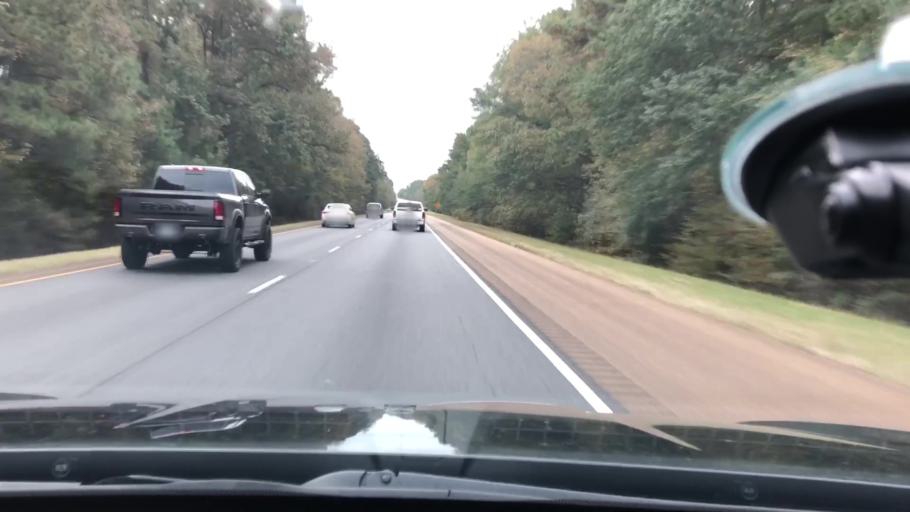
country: US
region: Arkansas
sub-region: Nevada County
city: Prescott
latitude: 33.8703
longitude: -93.3414
